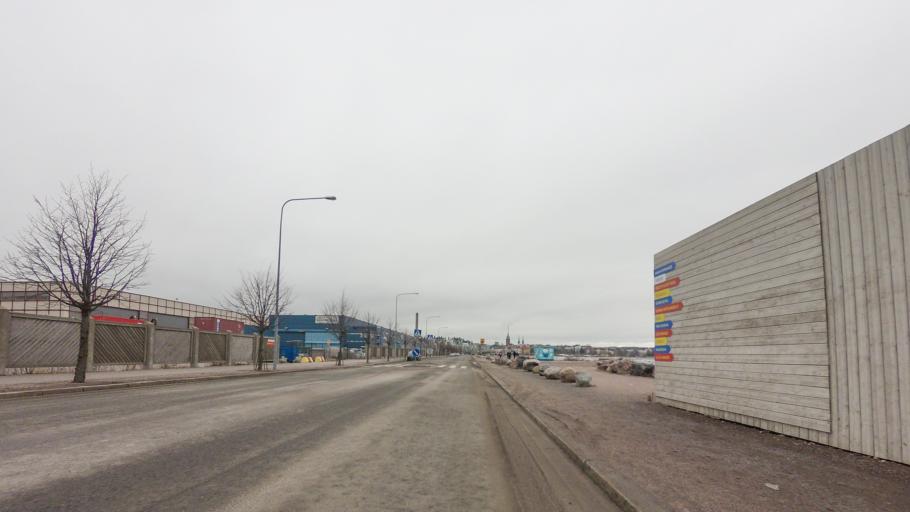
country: FI
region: Uusimaa
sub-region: Helsinki
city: Helsinki
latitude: 60.1490
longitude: 24.9269
